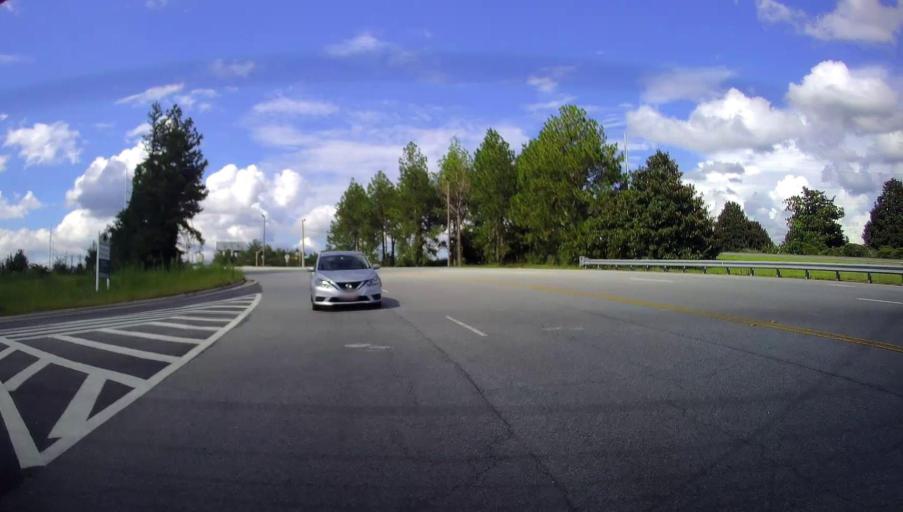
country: US
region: Georgia
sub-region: Muscogee County
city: Columbus
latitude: 32.5397
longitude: -84.8734
